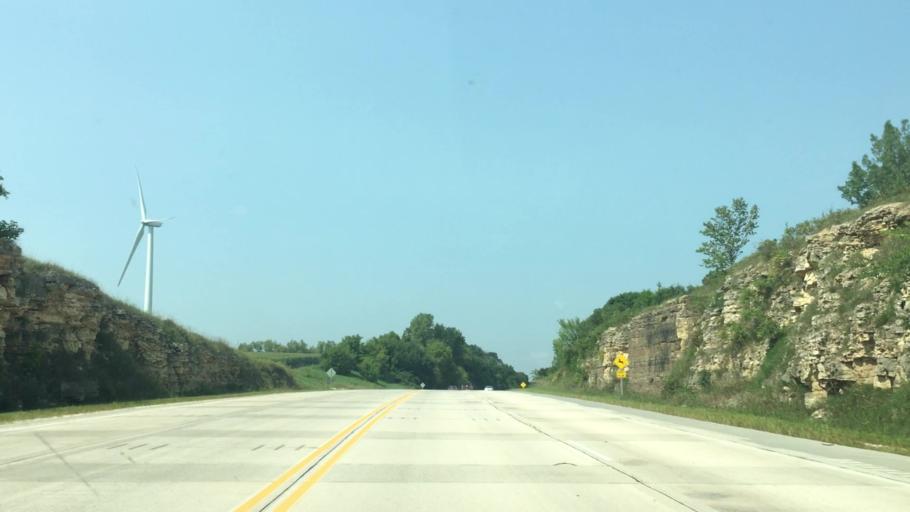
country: US
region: Iowa
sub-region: Winneshiek County
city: Decorah
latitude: 43.3049
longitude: -91.8150
